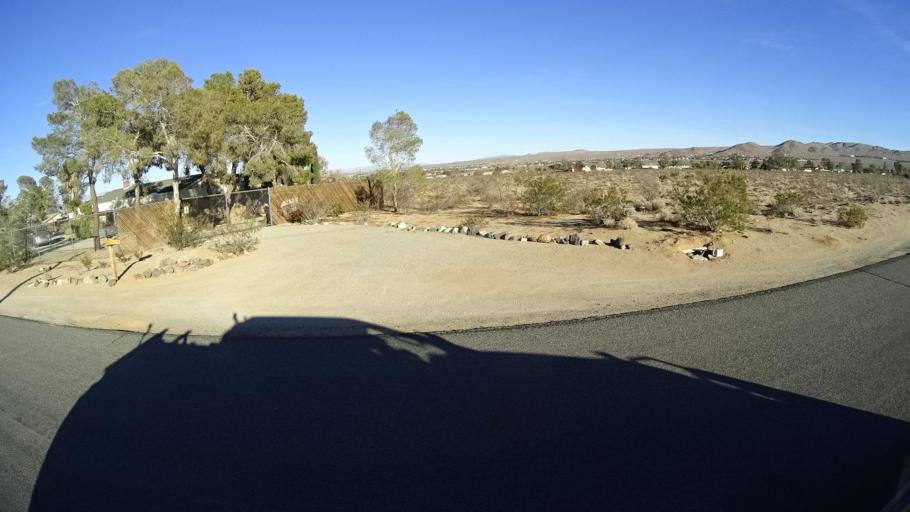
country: US
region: California
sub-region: Kern County
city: Ridgecrest
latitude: 35.5914
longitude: -117.6972
